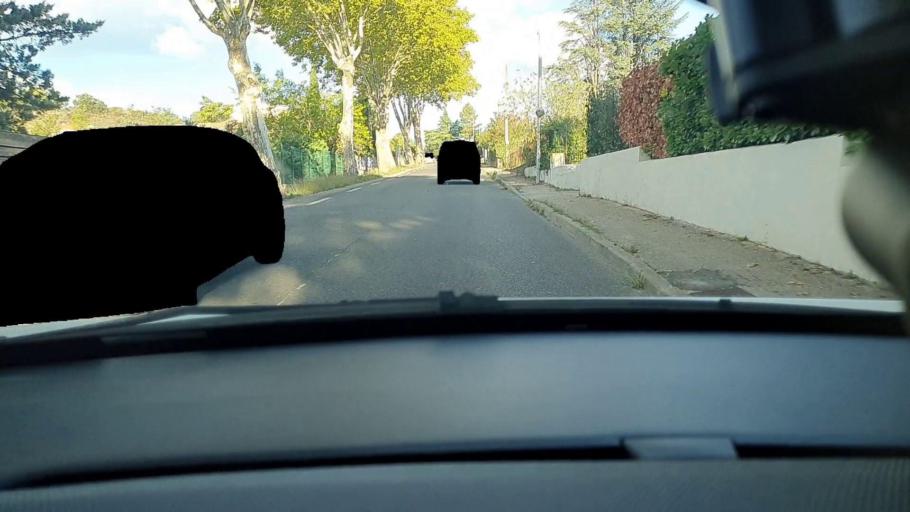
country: FR
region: Languedoc-Roussillon
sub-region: Departement du Gard
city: Saint-Ambroix
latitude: 44.2571
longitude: 4.2087
